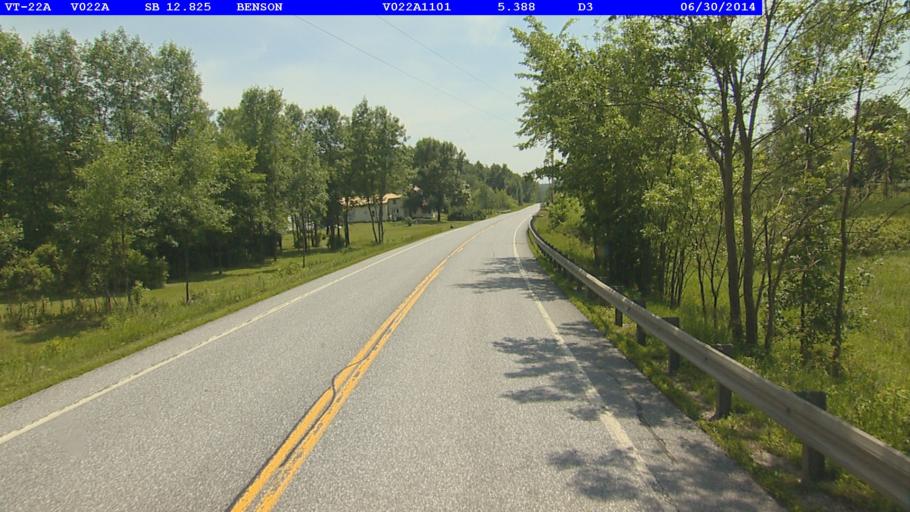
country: US
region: New York
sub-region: Essex County
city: Ticonderoga
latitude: 43.7451
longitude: -73.3071
